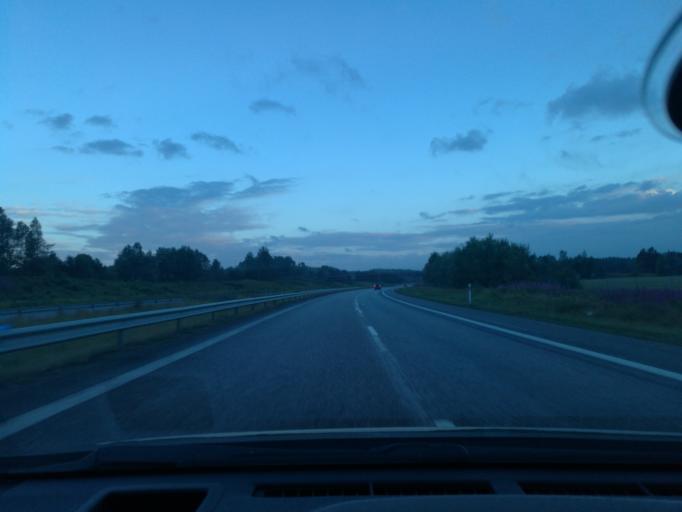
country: SE
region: Kronoberg
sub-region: Markaryds Kommun
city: Stromsnasbruk
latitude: 56.6459
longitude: 13.8032
